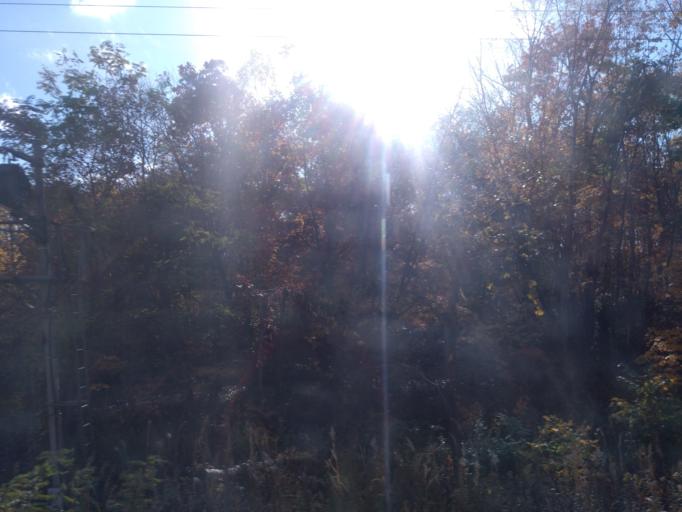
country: JP
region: Hokkaido
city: Kitahiroshima
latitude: 42.9951
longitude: 141.5406
